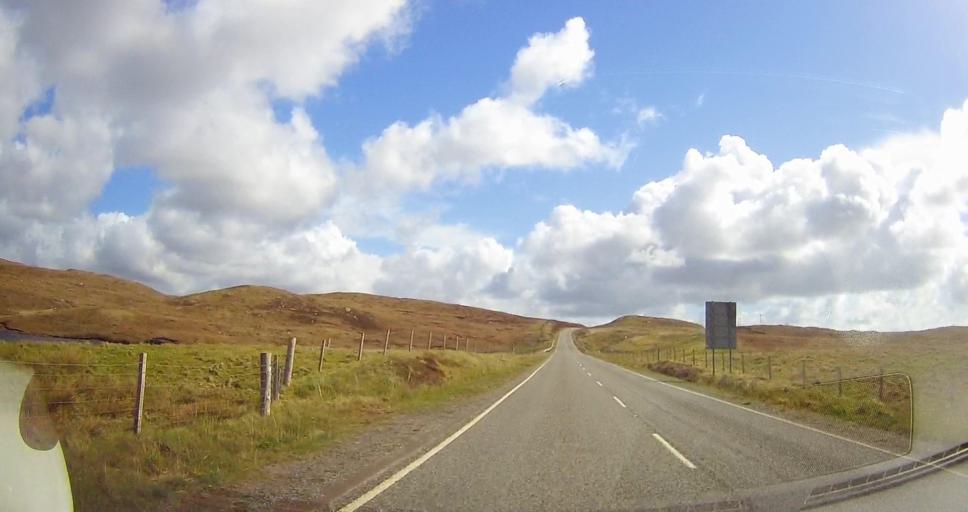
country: GB
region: Scotland
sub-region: Shetland Islands
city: Lerwick
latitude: 60.4753
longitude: -1.4083
